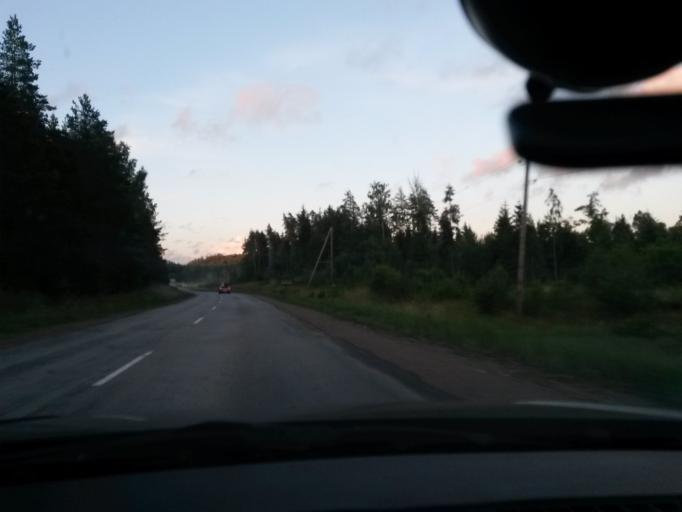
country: LV
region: Madonas Rajons
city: Madona
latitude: 56.8184
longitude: 26.1432
